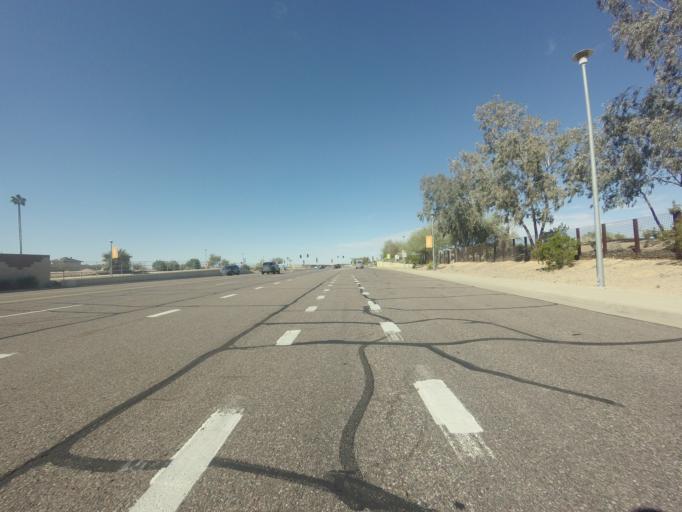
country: US
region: Arizona
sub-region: Maricopa County
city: Mesa
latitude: 33.4665
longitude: -111.7169
